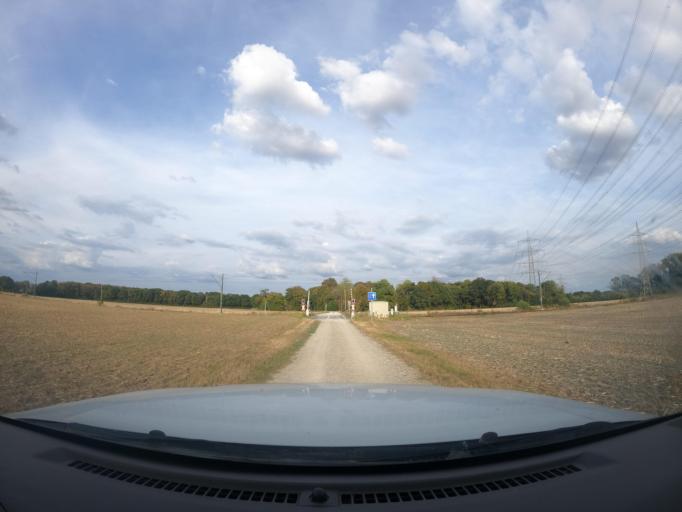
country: DE
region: North Rhine-Westphalia
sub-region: Regierungsbezirk Dusseldorf
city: Wesel
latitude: 51.6994
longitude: 6.6106
